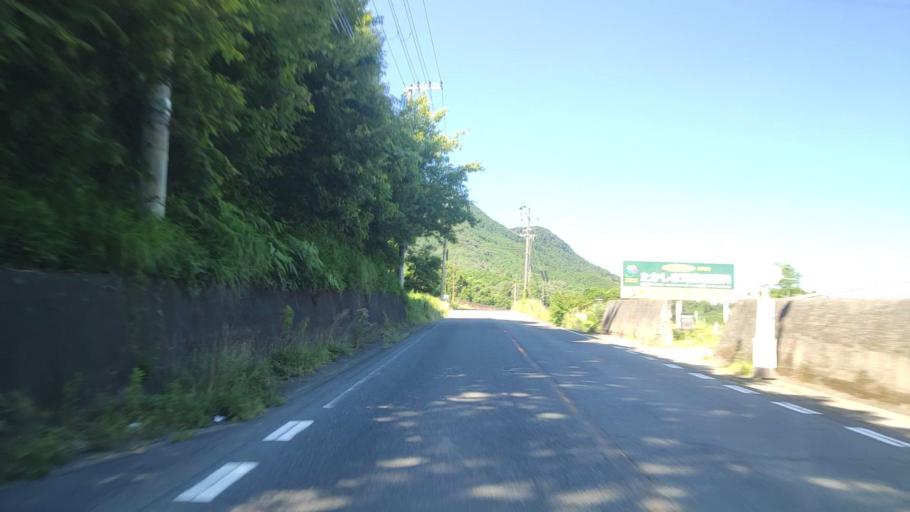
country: JP
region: Nara
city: Haibara-akanedai
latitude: 34.5465
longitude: 135.9604
